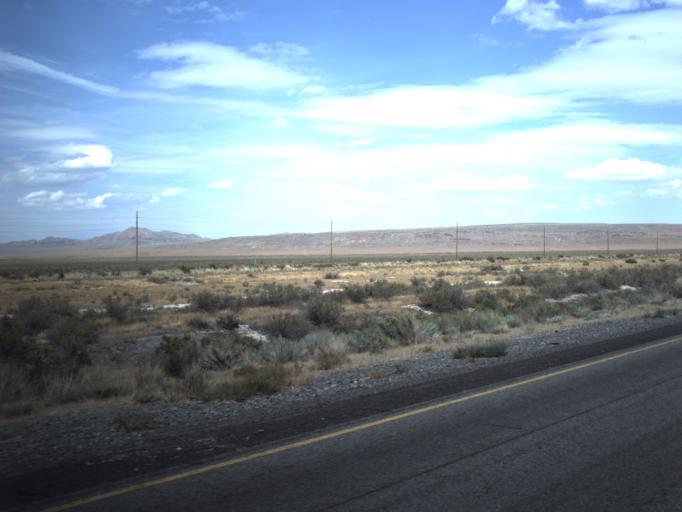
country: US
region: Utah
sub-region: Tooele County
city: Grantsville
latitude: 40.7412
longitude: -113.0784
